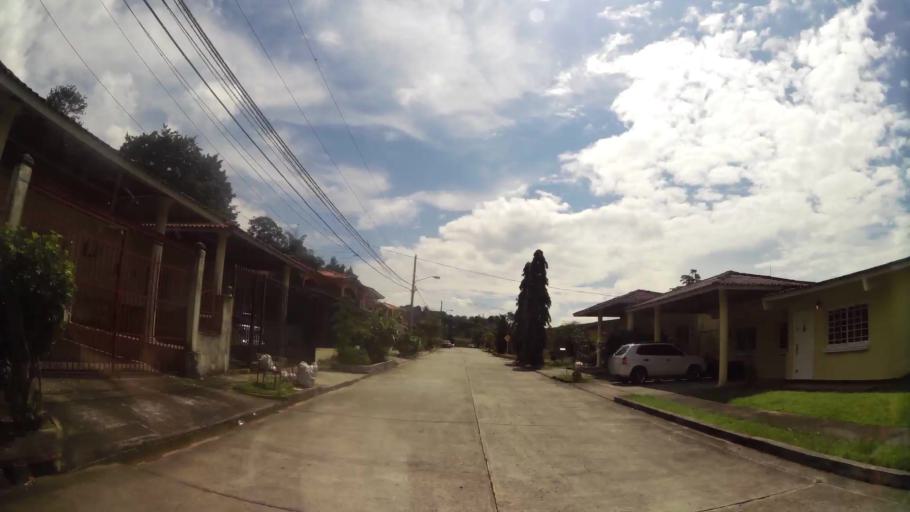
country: PA
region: Panama
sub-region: Distrito Arraijan
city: Arraijan
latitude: 8.9450
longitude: -79.6752
